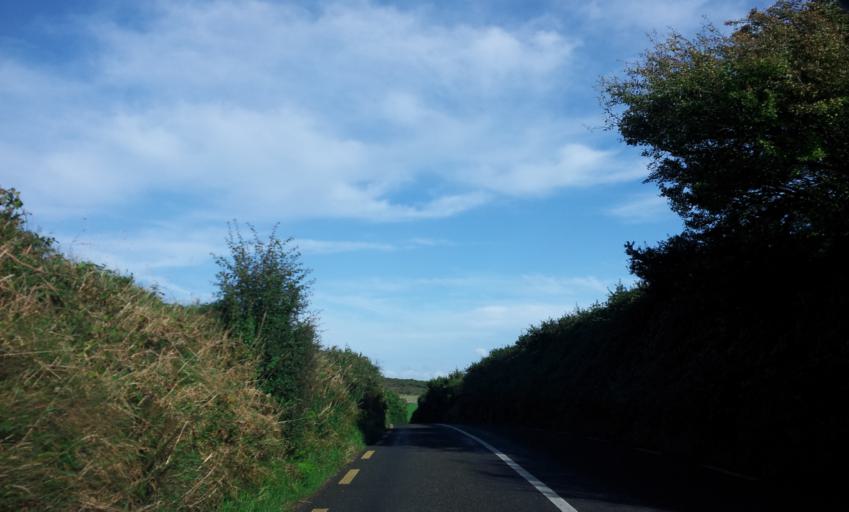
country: IE
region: Munster
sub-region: An Clar
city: Ennis
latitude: 52.9834
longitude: -9.1282
